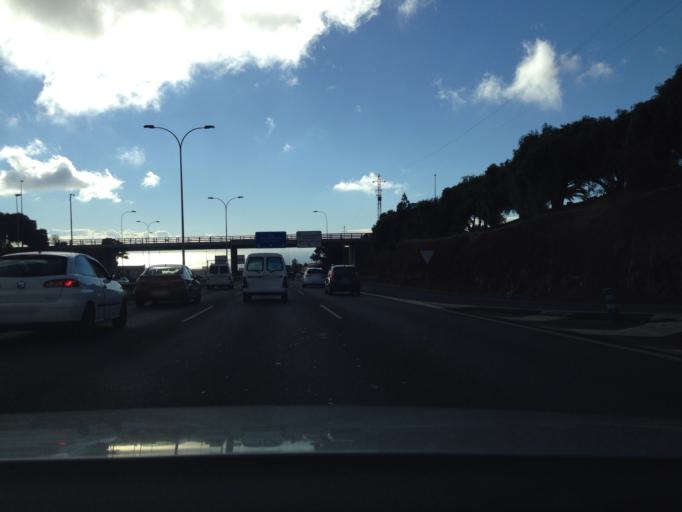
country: ES
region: Canary Islands
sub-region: Provincia de Santa Cruz de Tenerife
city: La Laguna
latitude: 28.4770
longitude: -16.3146
